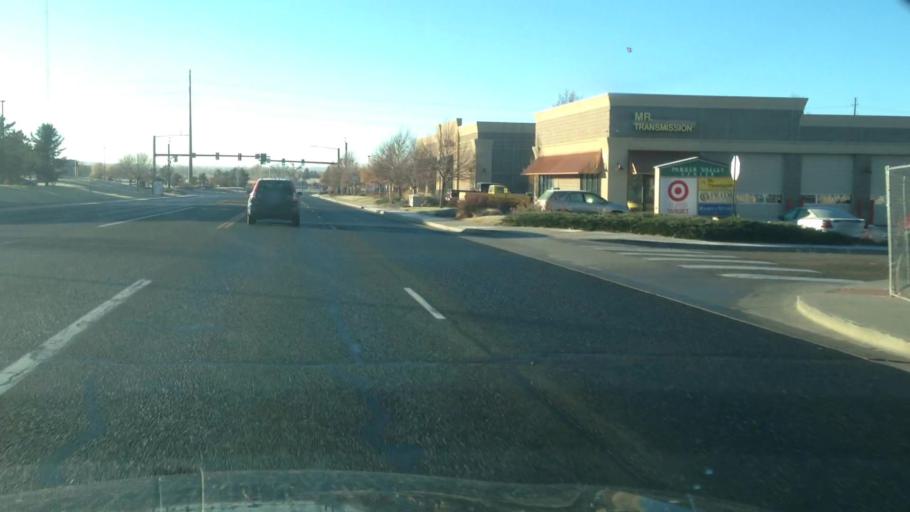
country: US
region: Colorado
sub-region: Douglas County
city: Parker
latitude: 39.5144
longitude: -104.7700
